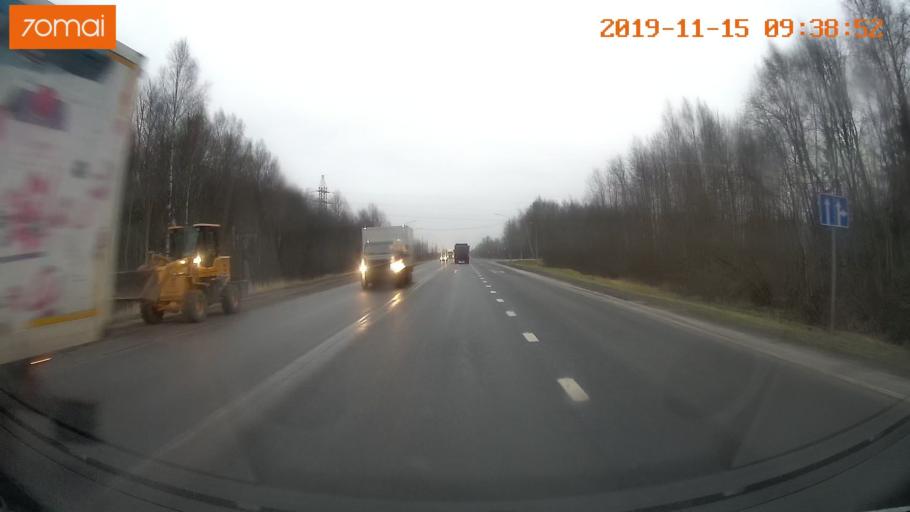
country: RU
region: Vologda
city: Sheksna
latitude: 59.2286
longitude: 38.4632
